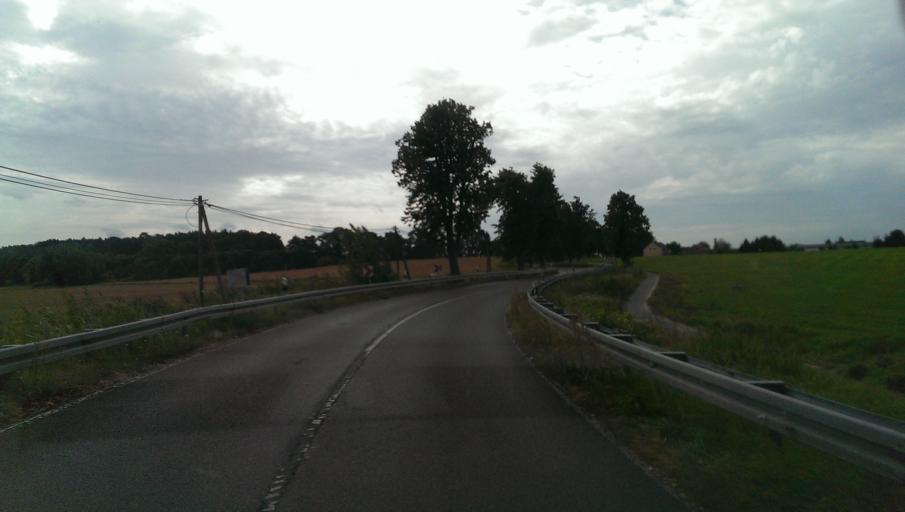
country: DE
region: Brandenburg
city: Trebbin
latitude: 52.2054
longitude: 13.2106
